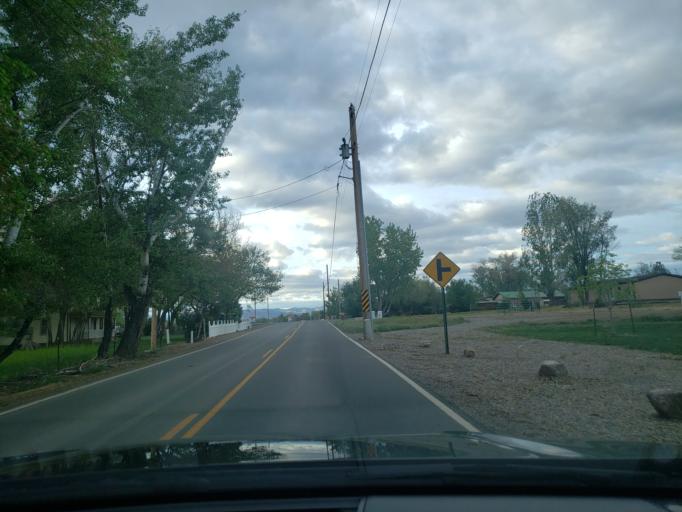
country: US
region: Colorado
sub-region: Mesa County
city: Fruita
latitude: 39.1810
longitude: -108.7290
